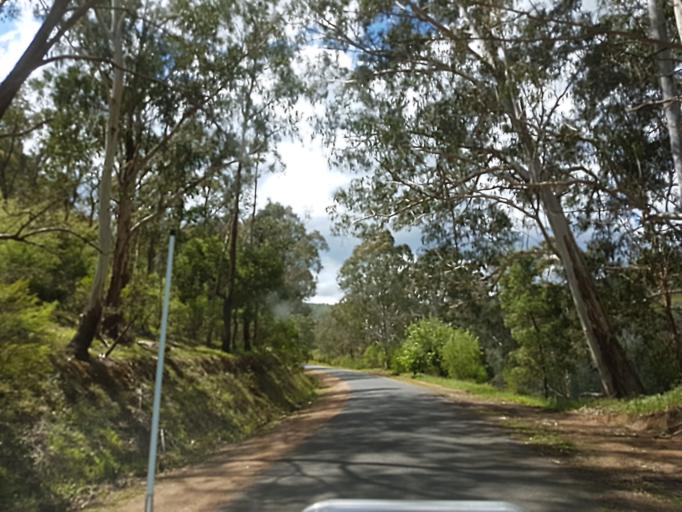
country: AU
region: Victoria
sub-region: East Gippsland
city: Bairnsdale
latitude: -37.4255
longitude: 147.2509
